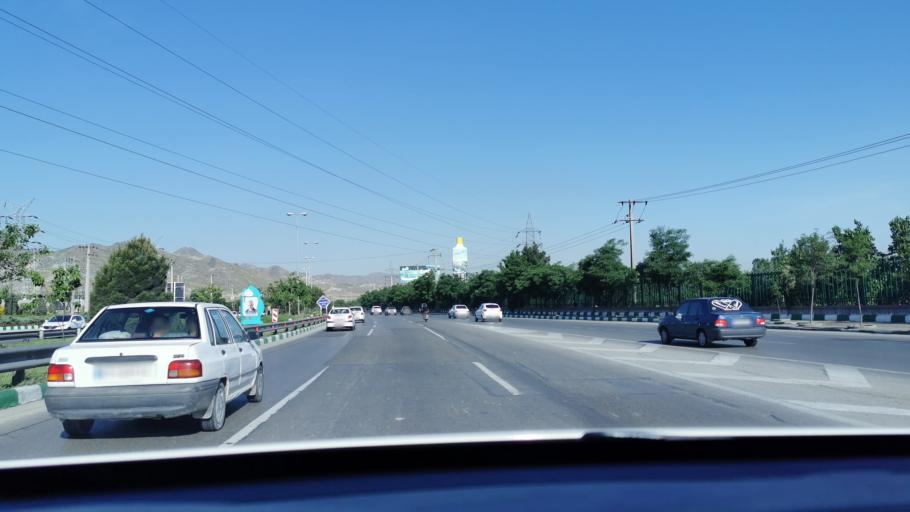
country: IR
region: Razavi Khorasan
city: Mashhad
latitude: 36.2569
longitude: 59.5954
